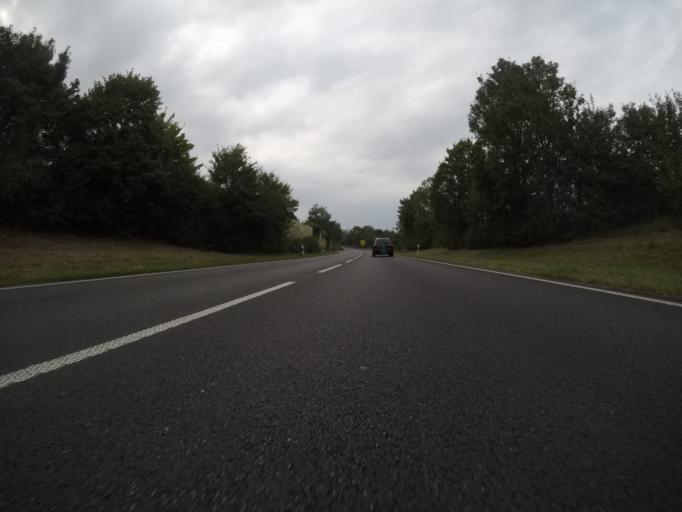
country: DE
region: Baden-Wuerttemberg
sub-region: Regierungsbezirk Stuttgart
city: Schwieberdingen
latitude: 48.8771
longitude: 9.0849
